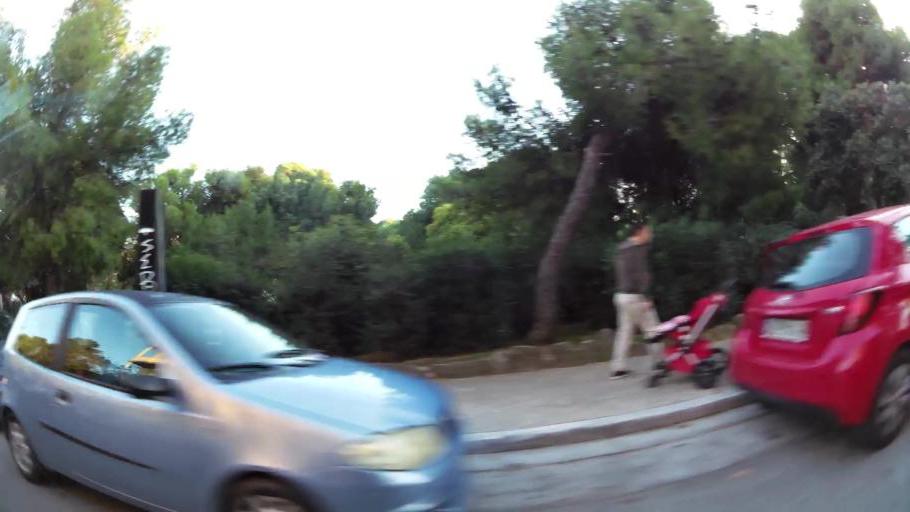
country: GR
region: Attica
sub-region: Nomarchia Athinas
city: Kifisia
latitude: 38.0752
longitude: 23.8207
